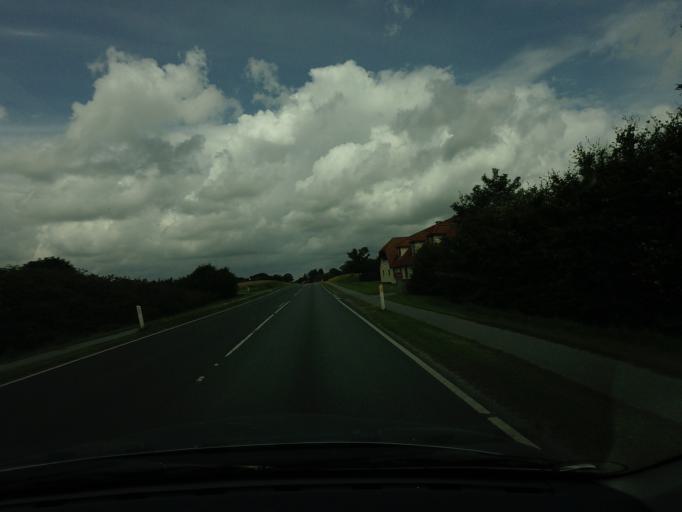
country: DK
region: North Denmark
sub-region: Hjorring Kommune
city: Tars
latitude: 57.3906
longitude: 10.1044
